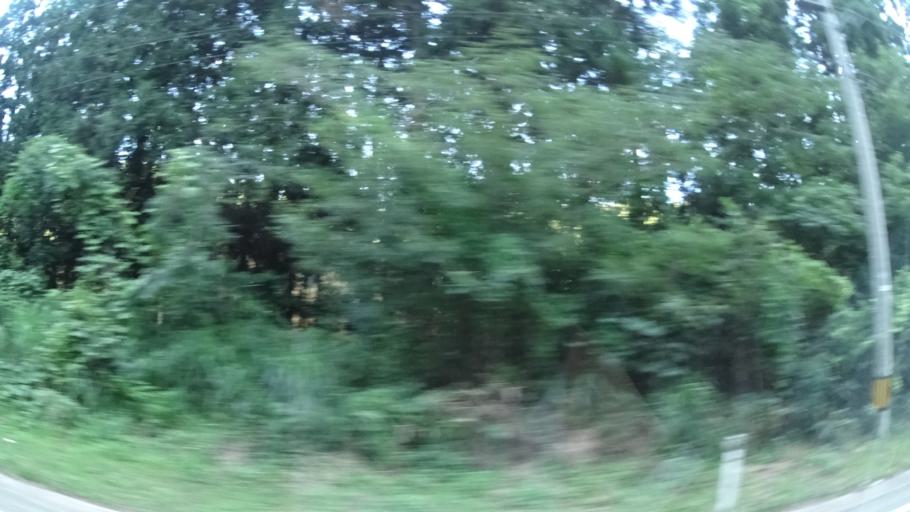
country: JP
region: Ishikawa
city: Nanao
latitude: 37.2855
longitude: 136.8891
